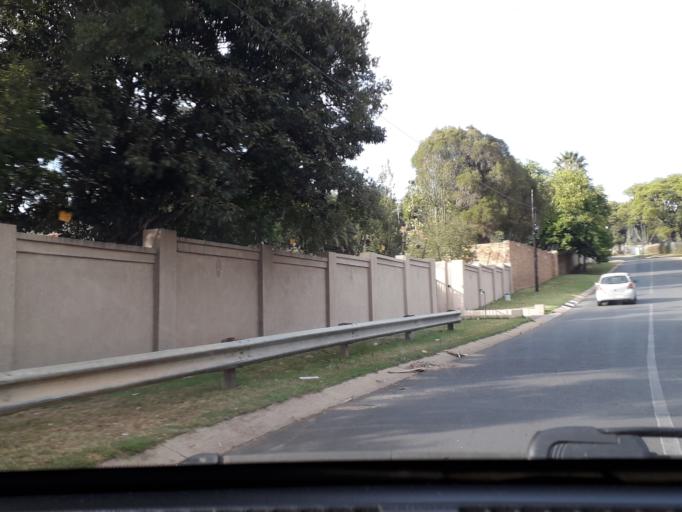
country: ZA
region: Gauteng
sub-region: City of Johannesburg Metropolitan Municipality
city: Modderfontein
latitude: -26.1172
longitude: 28.0798
